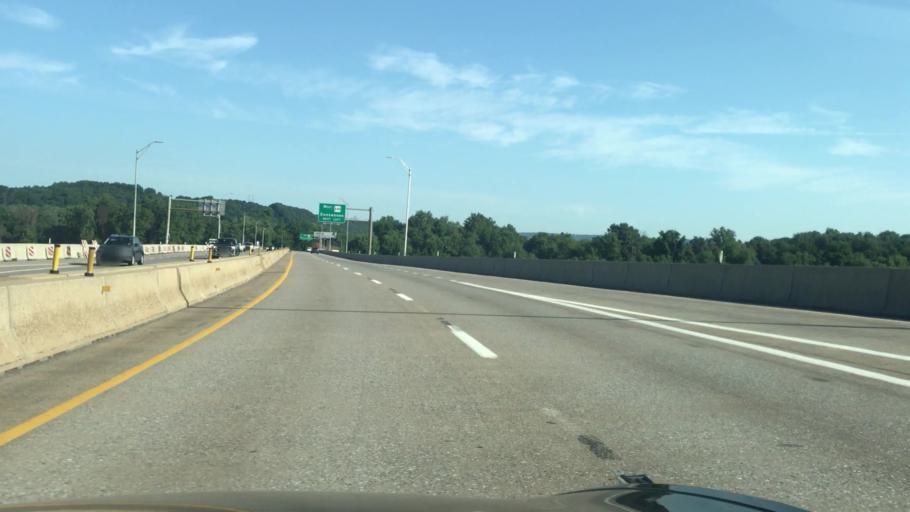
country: US
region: Pennsylvania
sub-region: Perry County
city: Duncannon
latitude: 40.3983
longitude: -77.0082
